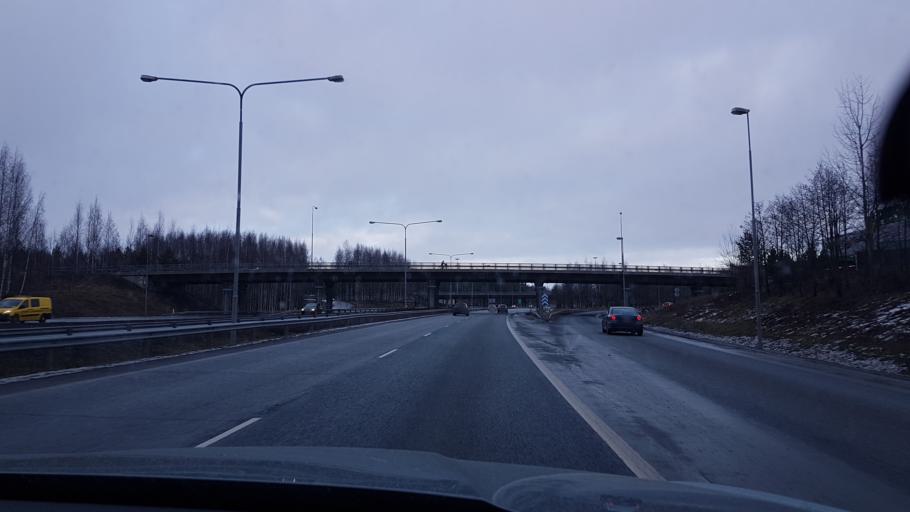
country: FI
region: Pirkanmaa
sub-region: Tampere
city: Tampere
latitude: 61.4962
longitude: 23.8804
